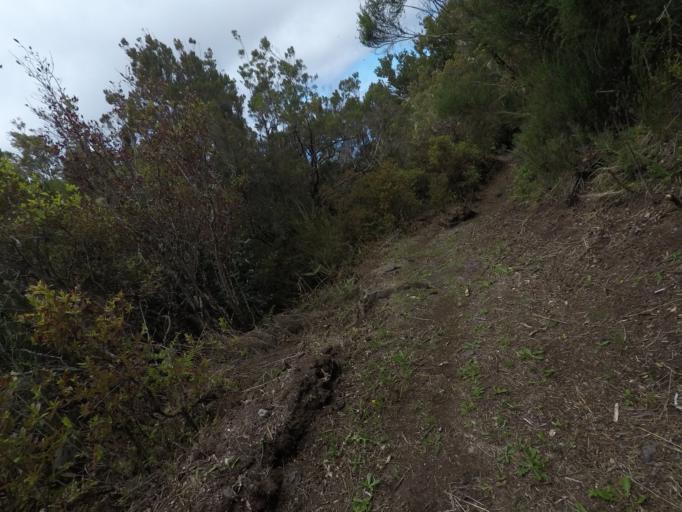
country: PT
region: Madeira
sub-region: Camara de Lobos
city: Curral das Freiras
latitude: 32.7675
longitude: -16.9755
